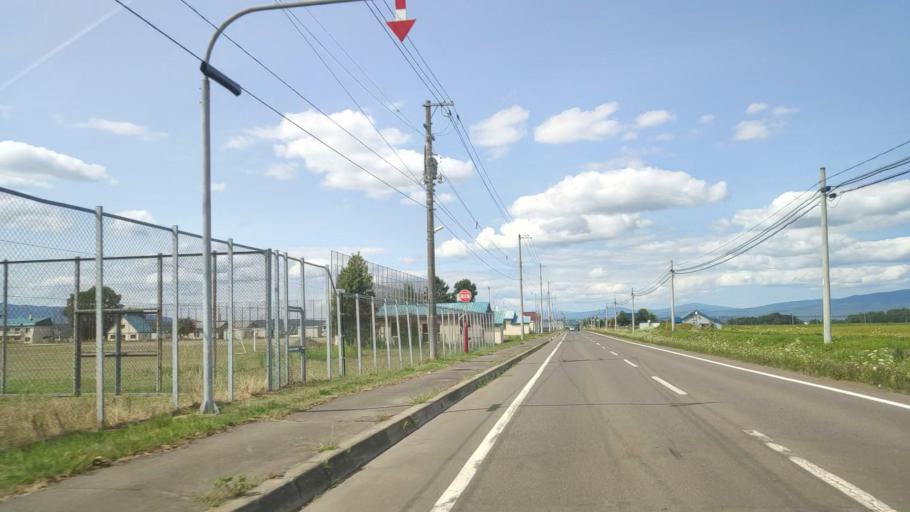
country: JP
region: Hokkaido
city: Nayoro
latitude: 44.2919
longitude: 142.4294
